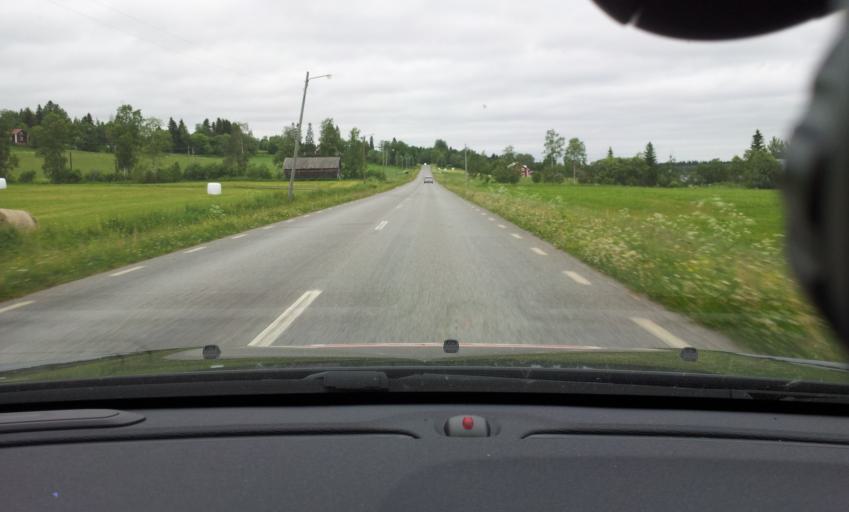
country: SE
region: Jaemtland
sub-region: Krokoms Kommun
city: Krokom
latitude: 63.1459
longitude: 14.1739
